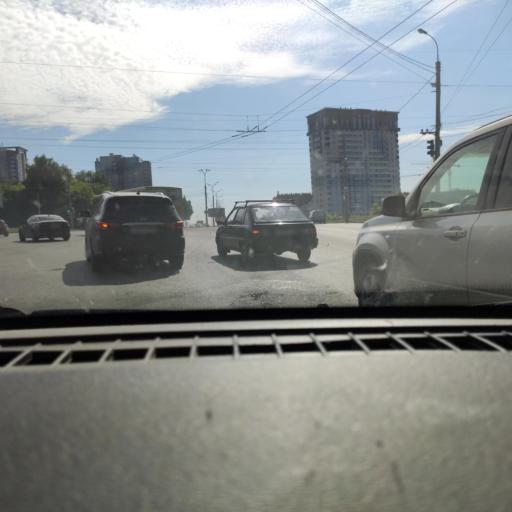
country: RU
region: Udmurtiya
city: Izhevsk
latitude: 56.8714
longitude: 53.2555
